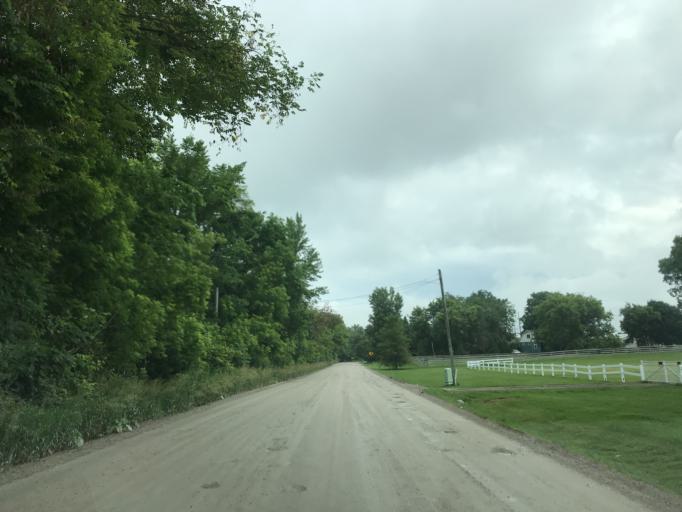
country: US
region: Michigan
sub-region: Oakland County
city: South Lyon
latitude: 42.4300
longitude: -83.6258
